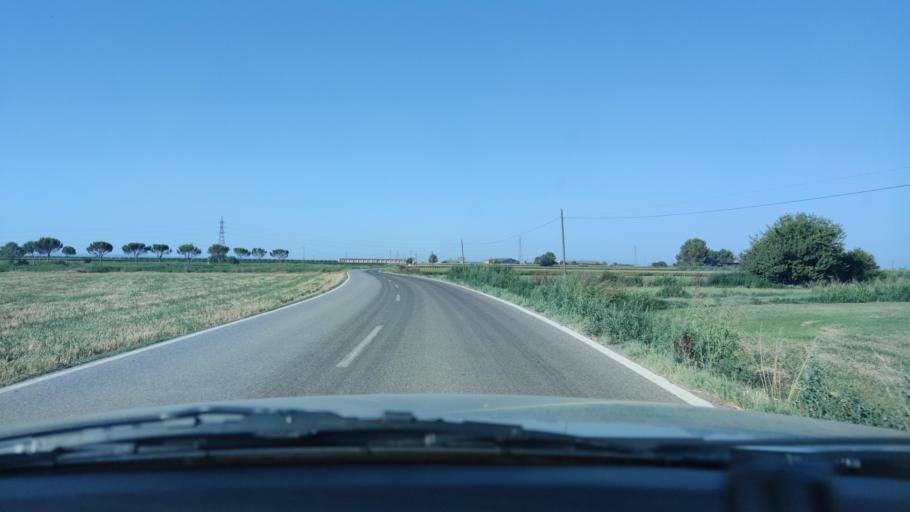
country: ES
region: Catalonia
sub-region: Provincia de Lleida
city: Bellvis
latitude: 41.6557
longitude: 0.8056
